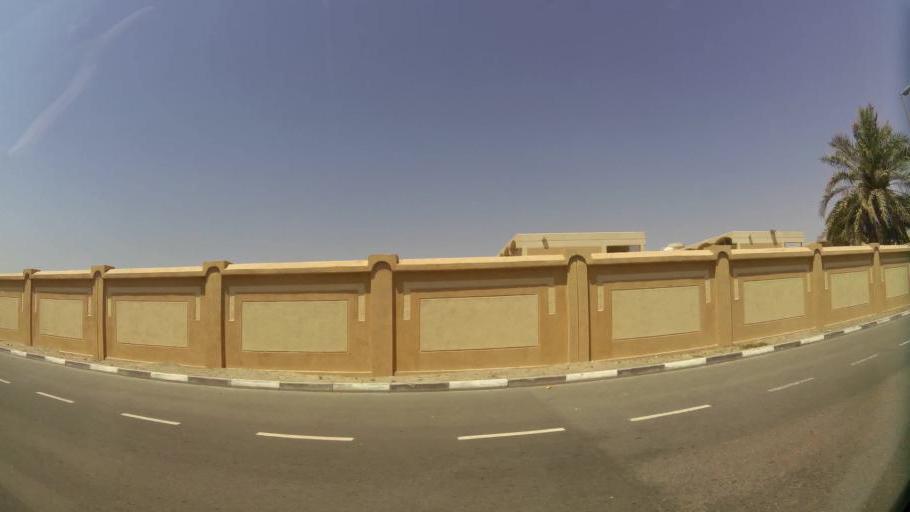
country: AE
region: Ash Shariqah
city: Sharjah
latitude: 25.2930
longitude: 55.3462
